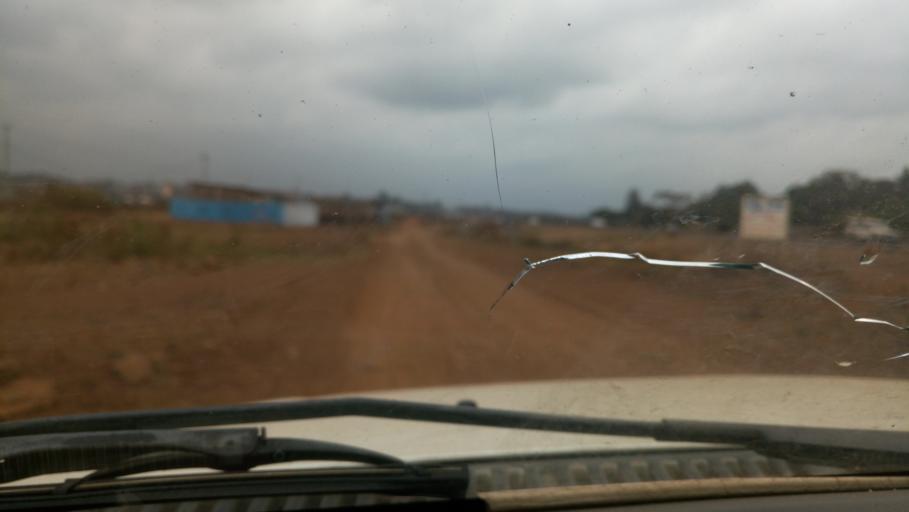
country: KE
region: Kiambu
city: Kiambu
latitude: -1.1996
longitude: 36.8964
